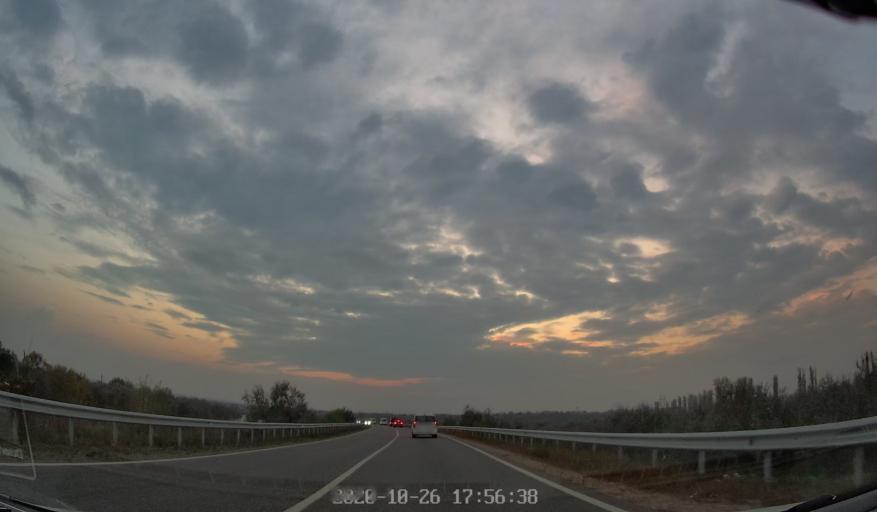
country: UA
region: Odessa
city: Bilyayivka
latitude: 46.4121
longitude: 30.1134
